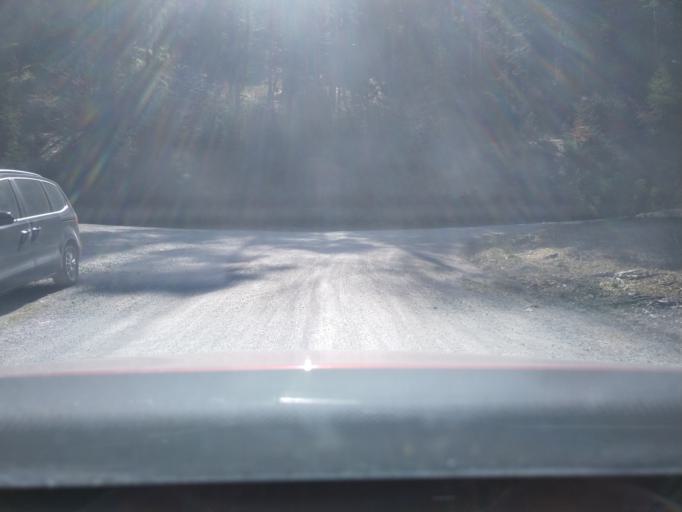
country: AT
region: Lower Austria
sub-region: Politischer Bezirk Neunkirchen
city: Puchberg am Schneeberg
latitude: 47.8125
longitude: 15.8435
